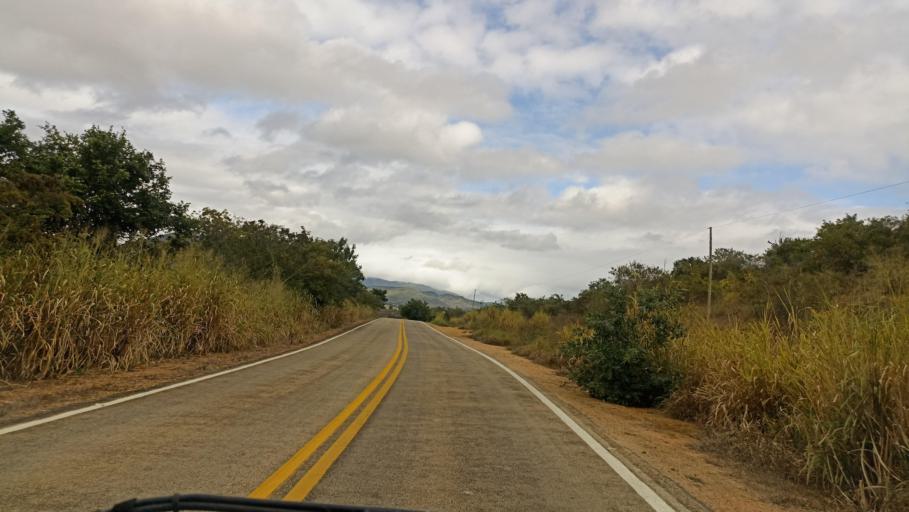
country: BR
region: Minas Gerais
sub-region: Joaima
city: Joaima
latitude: -16.6933
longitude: -40.9580
